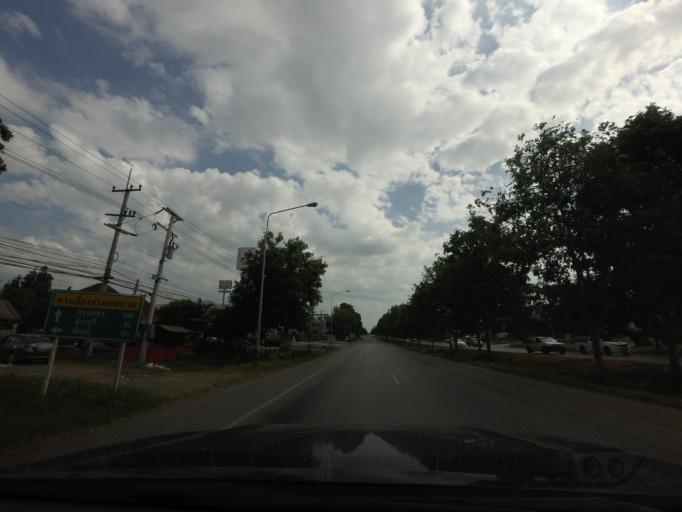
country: TH
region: Lop Buri
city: Chai Badan
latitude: 15.2232
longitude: 101.1274
